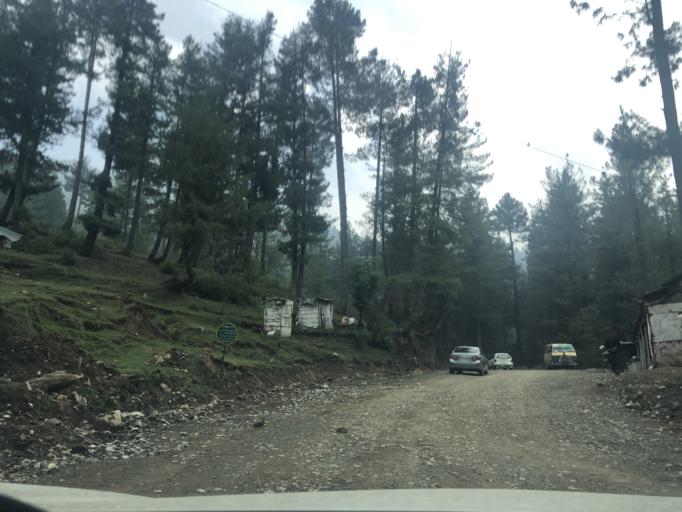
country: PK
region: Khyber Pakhtunkhwa
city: Alpurai
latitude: 34.8168
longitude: 72.5746
